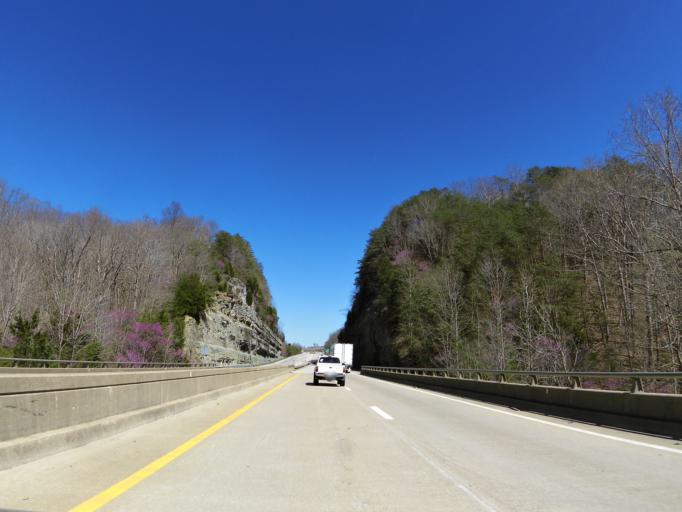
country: US
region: Kentucky
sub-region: Pulaski County
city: Somerset
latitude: 37.0978
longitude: -84.6893
